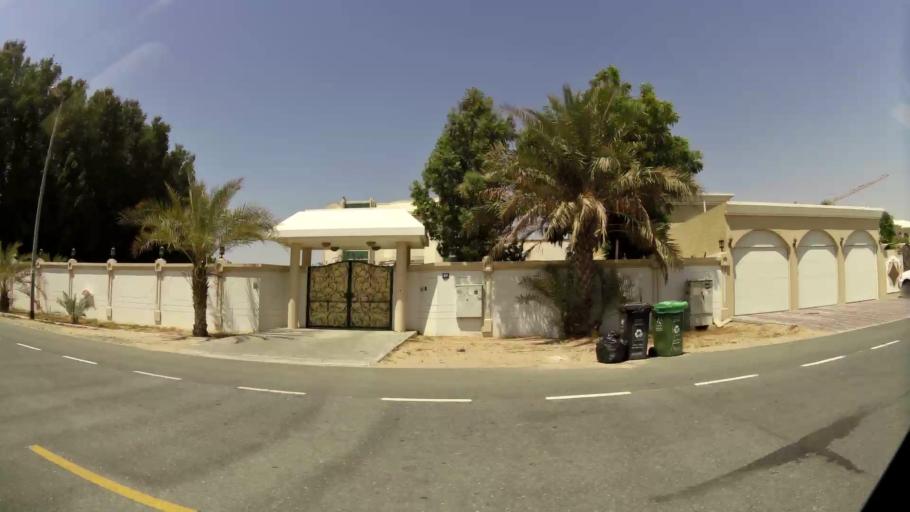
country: AE
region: Dubai
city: Dubai
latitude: 25.1043
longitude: 55.2258
